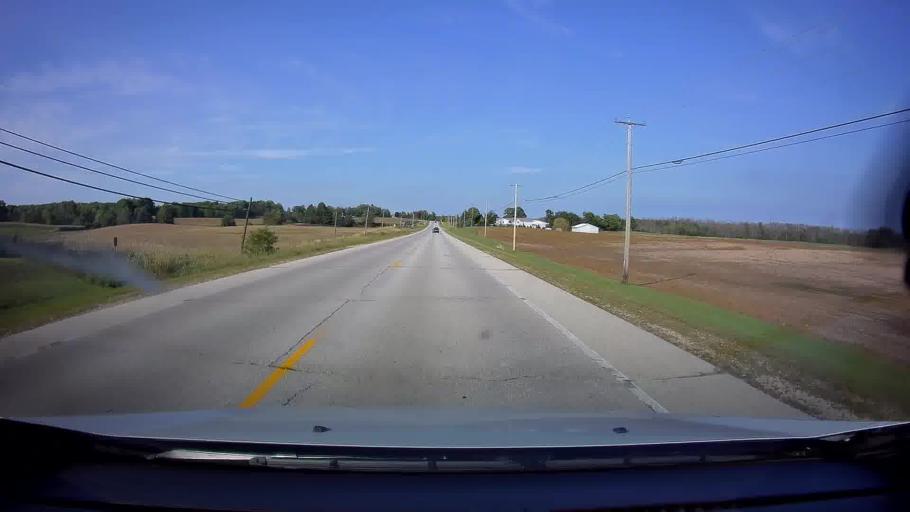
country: US
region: Wisconsin
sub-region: Door County
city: Sturgeon Bay
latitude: 44.9015
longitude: -87.2796
